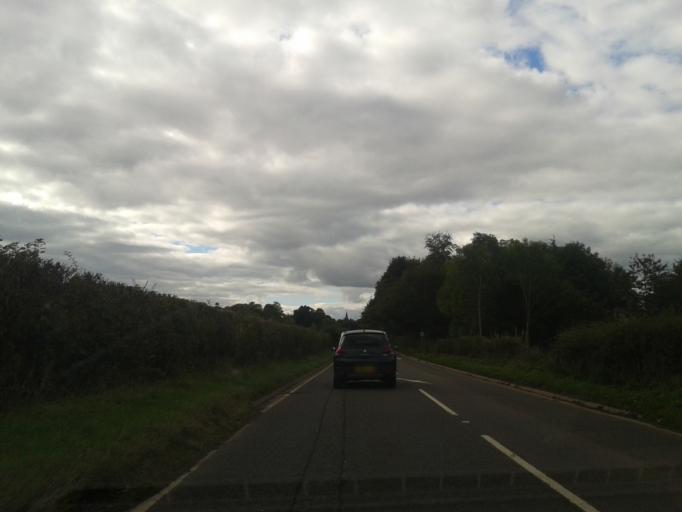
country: GB
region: Scotland
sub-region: Fife
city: Ladybank
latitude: 56.3046
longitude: -3.0906
